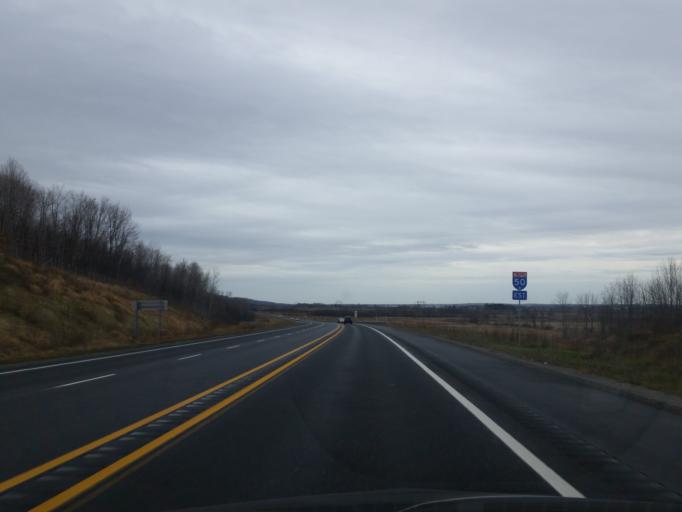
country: CA
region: Quebec
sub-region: Outaouais
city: Papineauville
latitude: 45.6550
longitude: -74.8575
